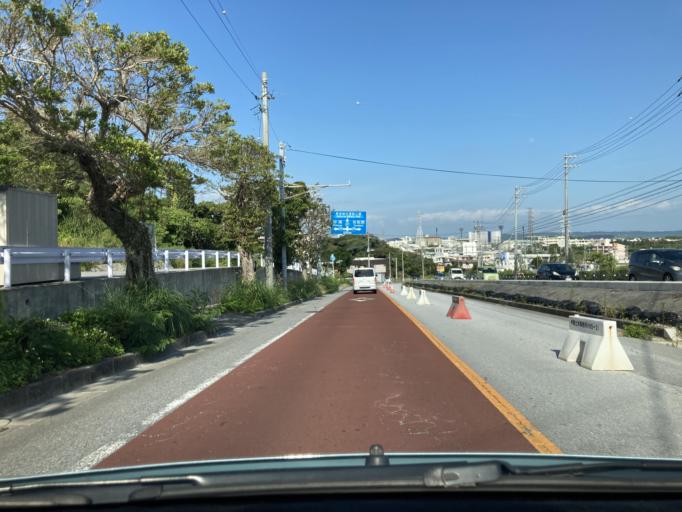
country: JP
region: Okinawa
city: Okinawa
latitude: 26.3021
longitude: 127.8064
